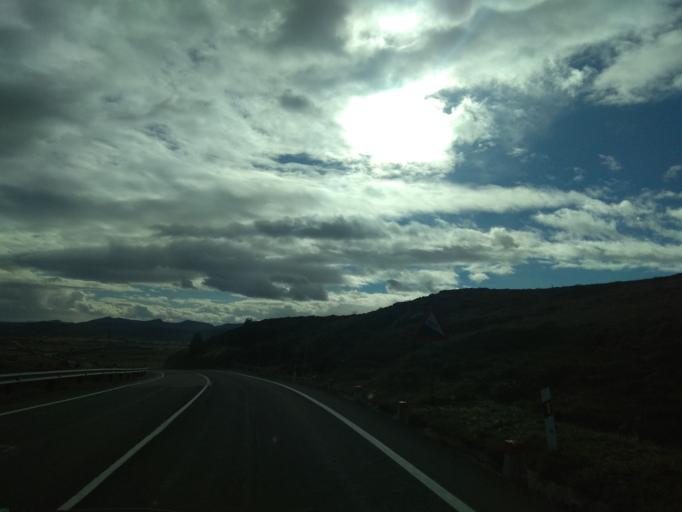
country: ES
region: Castille and Leon
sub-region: Provincia de Burgos
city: Arija
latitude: 43.0355
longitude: -3.8673
